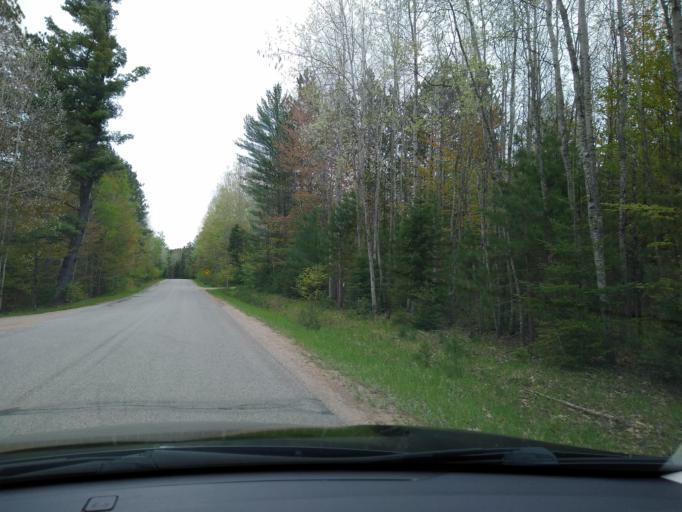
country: US
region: Michigan
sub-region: Delta County
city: Gladstone
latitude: 45.8896
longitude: -87.0470
